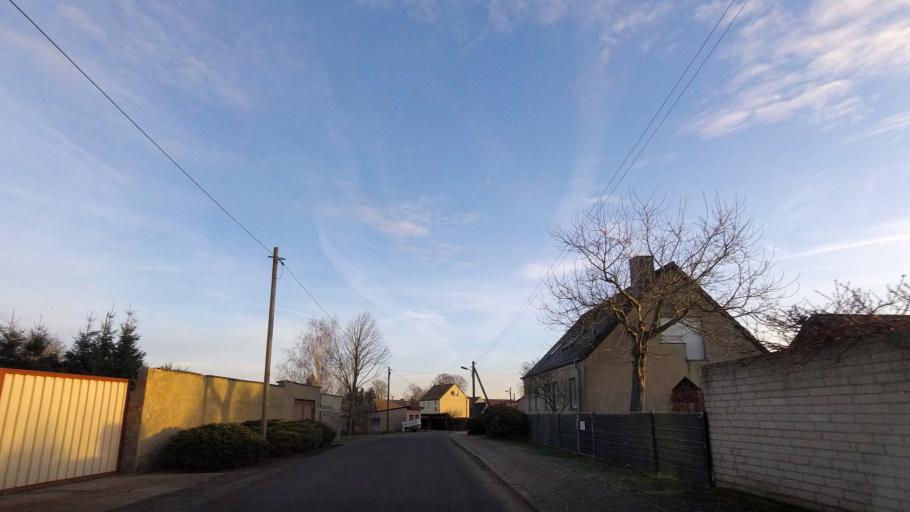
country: DE
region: Brandenburg
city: Niedergorsdorf
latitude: 51.9696
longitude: 12.9643
